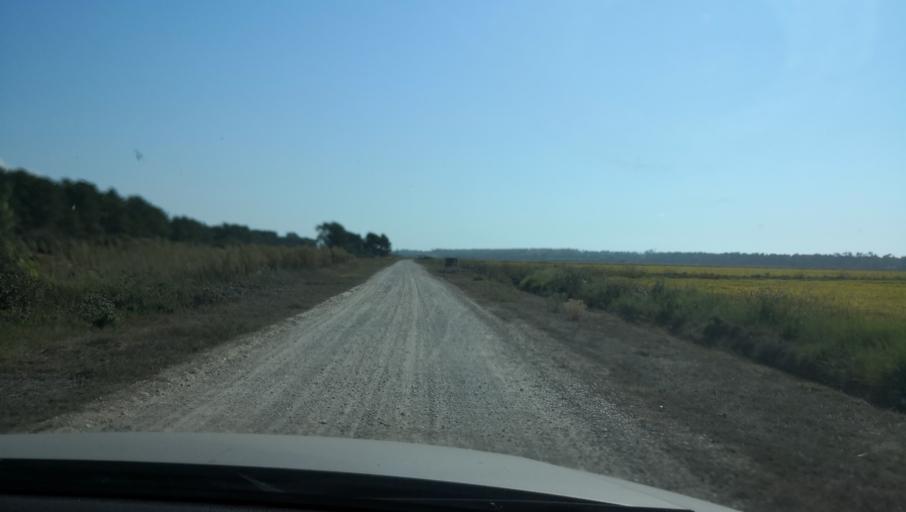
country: PT
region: Setubal
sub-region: Setubal
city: Setubal
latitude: 38.3959
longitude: -8.7882
